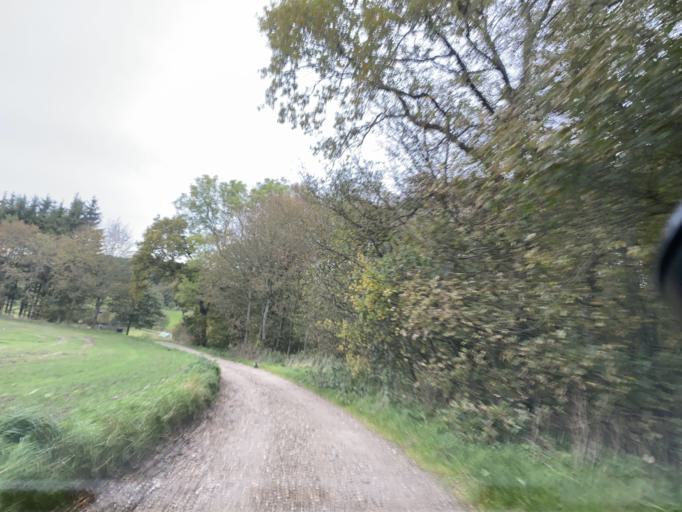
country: DK
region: Central Jutland
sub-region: Favrskov Kommune
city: Hammel
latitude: 56.1935
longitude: 9.7822
